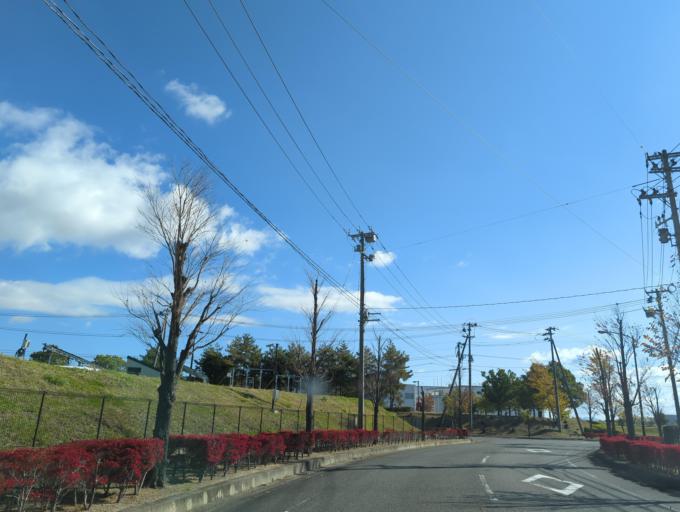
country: JP
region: Fukushima
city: Koriyama
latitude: 37.4492
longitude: 140.3144
